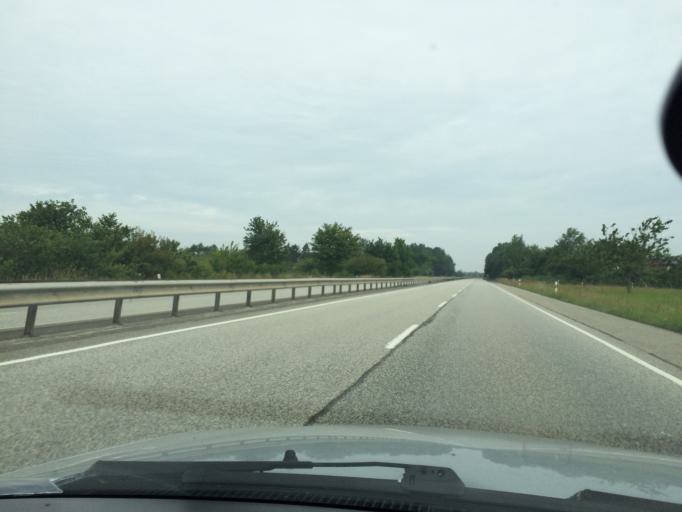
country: DE
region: Schleswig-Holstein
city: Flensburg
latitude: 54.7741
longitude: 9.4143
